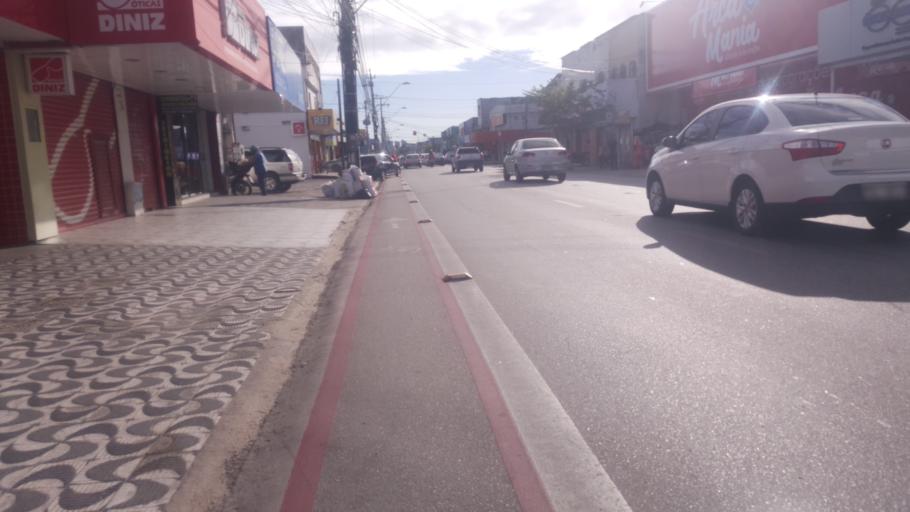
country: BR
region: Ceara
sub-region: Fortaleza
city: Fortaleza
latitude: -3.7637
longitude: -38.5477
